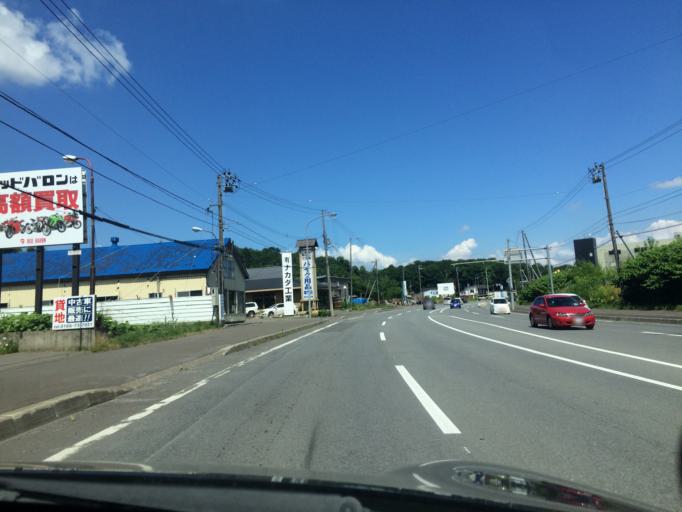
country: JP
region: Hokkaido
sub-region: Asahikawa-shi
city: Asahikawa
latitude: 43.7677
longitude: 142.2827
